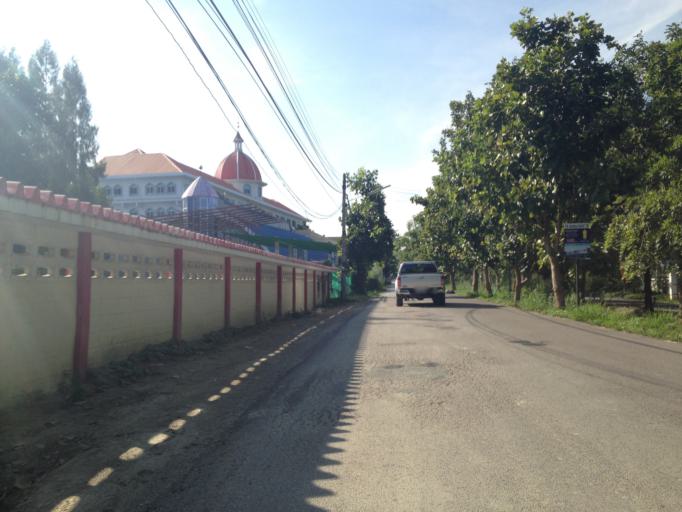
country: TH
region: Chiang Mai
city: Chiang Mai
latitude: 18.7391
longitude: 98.9550
